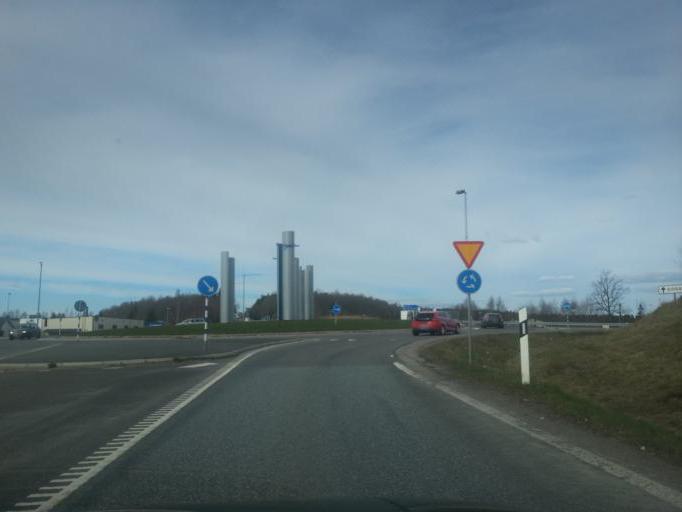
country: SE
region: Joenkoeping
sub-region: Habo Kommun
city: Habo
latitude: 57.8984
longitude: 14.1057
